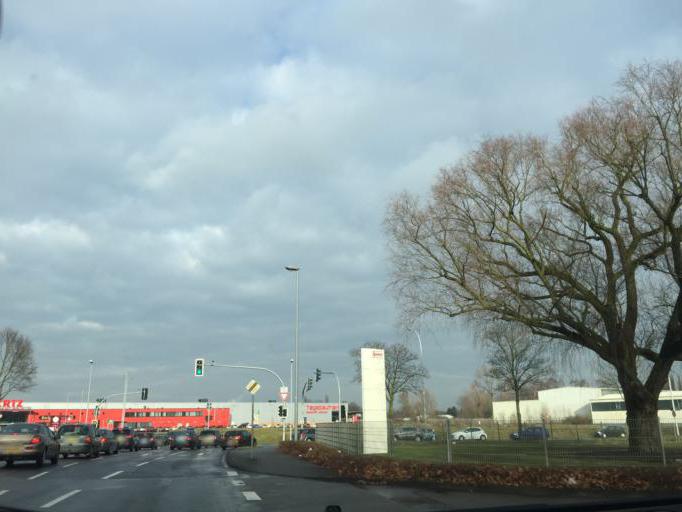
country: DE
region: North Rhine-Westphalia
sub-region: Regierungsbezirk Dusseldorf
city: Kleve
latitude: 51.7993
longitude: 6.1400
